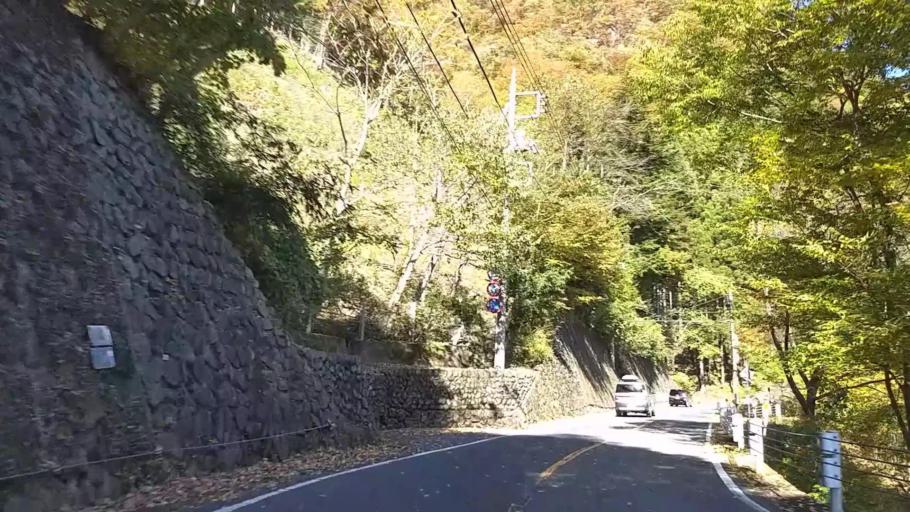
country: JP
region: Yamanashi
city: Otsuki
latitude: 35.7668
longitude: 138.9936
